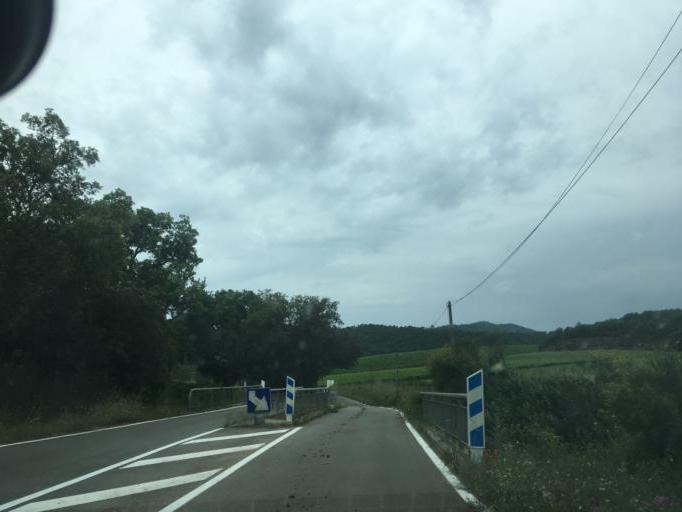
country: FR
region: Provence-Alpes-Cote d'Azur
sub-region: Departement du Var
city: La Londe-les-Maures
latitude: 43.2002
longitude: 6.2130
